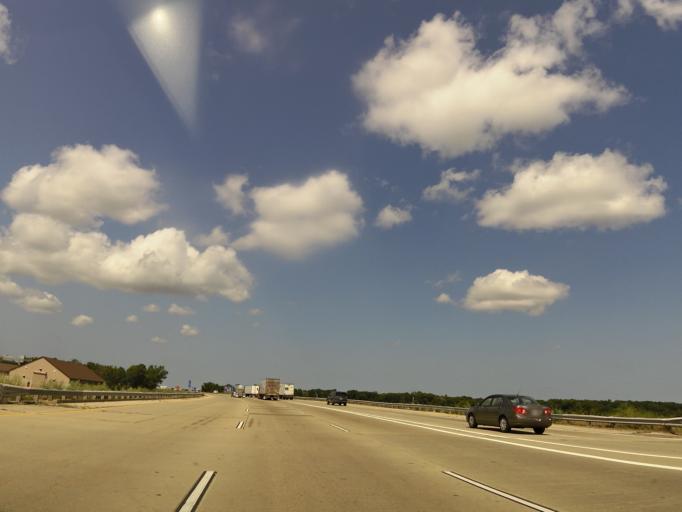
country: US
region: Wisconsin
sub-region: Dane County
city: Monona
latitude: 43.1068
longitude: -89.2824
